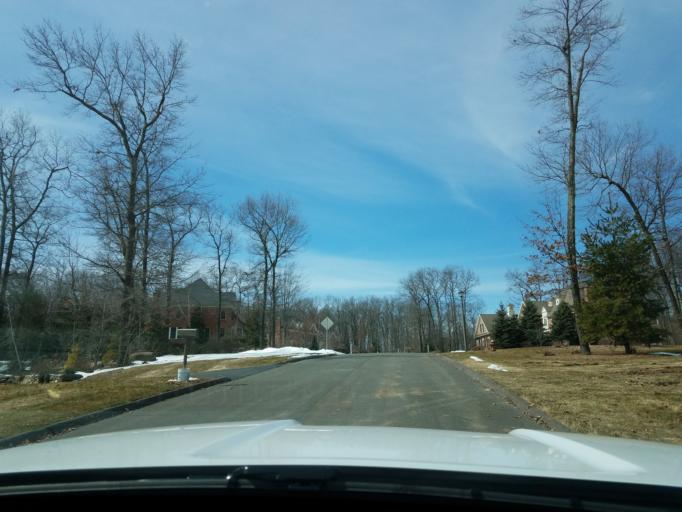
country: US
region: Connecticut
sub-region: Hartford County
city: Collinsville
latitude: 41.8104
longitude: -72.8994
